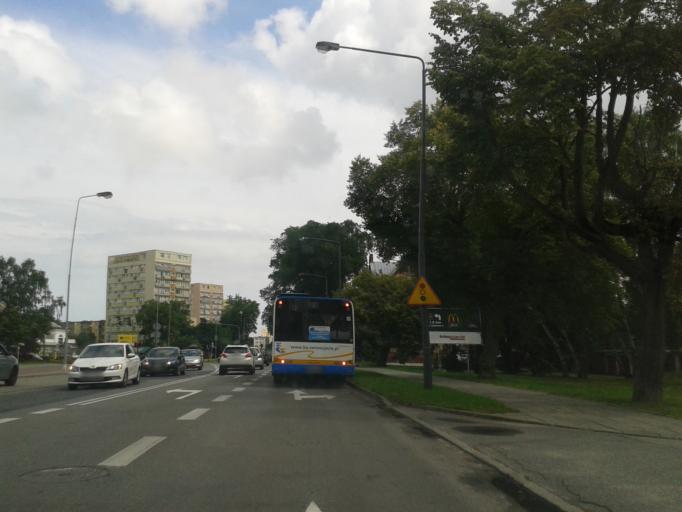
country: PL
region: West Pomeranian Voivodeship
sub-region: Swinoujscie
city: Swinoujscie
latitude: 53.9017
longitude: 14.2364
